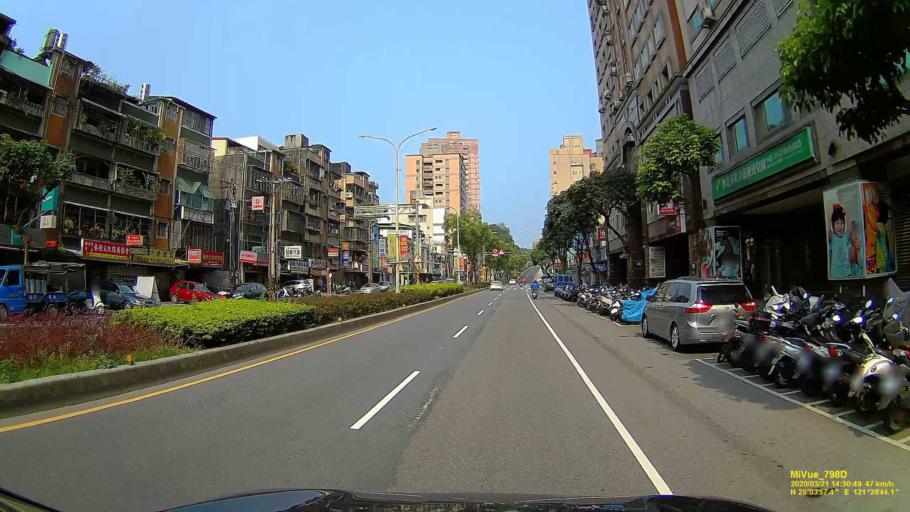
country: TW
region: Taiwan
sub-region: Keelung
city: Keelung
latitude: 25.0660
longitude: 121.6624
